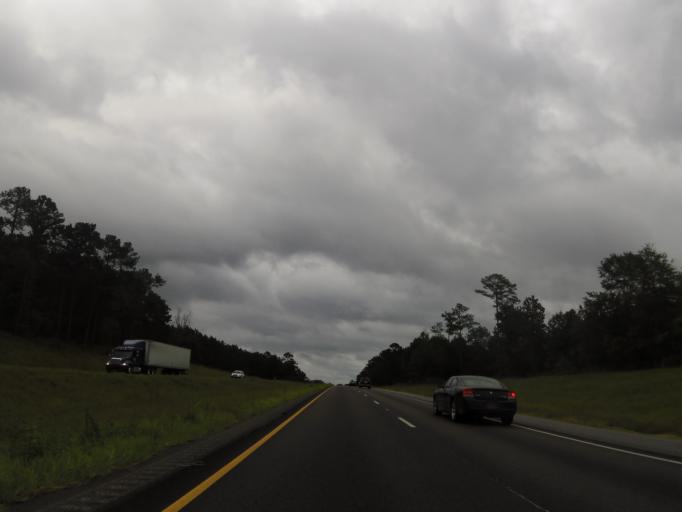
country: US
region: Alabama
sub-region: Conecuh County
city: Evergreen
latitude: 31.3478
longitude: -87.0896
